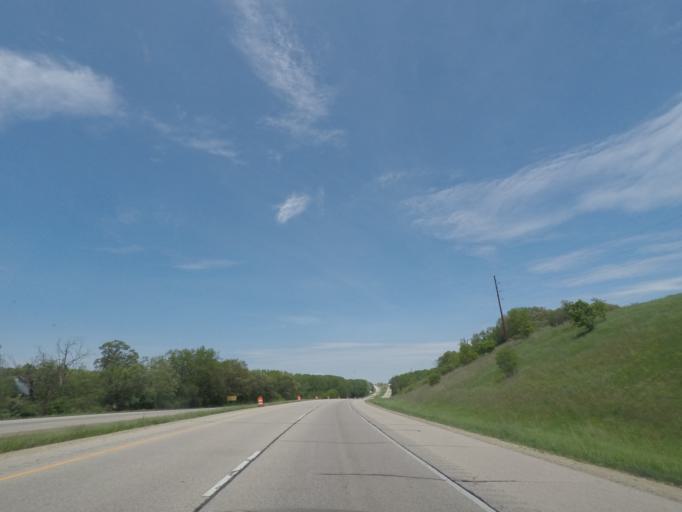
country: US
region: Wisconsin
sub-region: Dane County
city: Oregon
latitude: 42.9606
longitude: -89.3875
